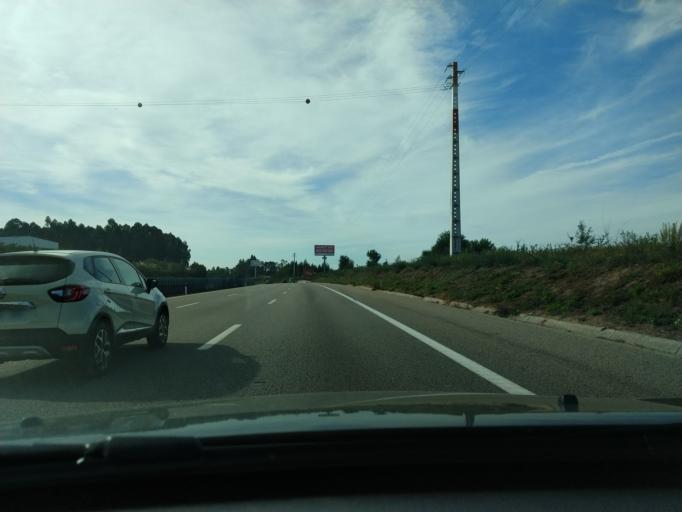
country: PT
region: Aveiro
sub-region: Santa Maria da Feira
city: Rio Meao
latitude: 40.9472
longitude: -8.5737
